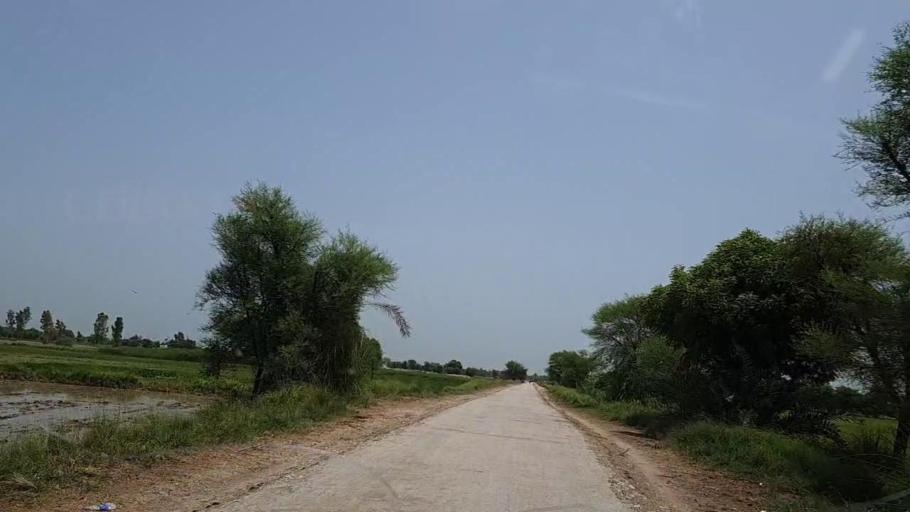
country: PK
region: Sindh
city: Tharu Shah
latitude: 26.9533
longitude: 68.0856
